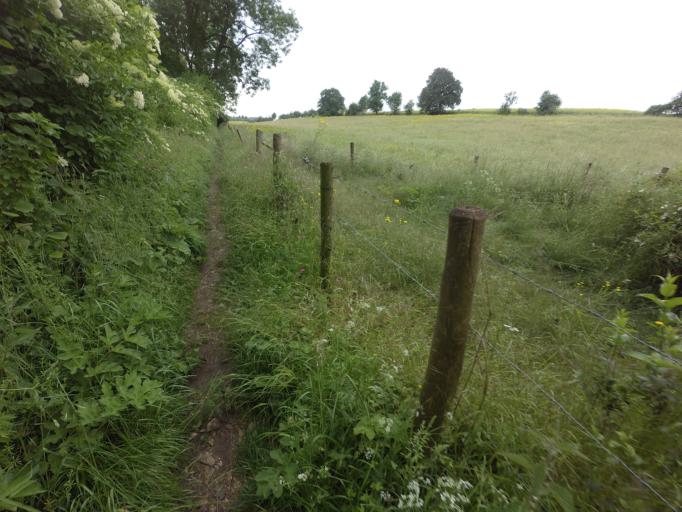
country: NL
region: Limburg
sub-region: Gemeente Voerendaal
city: Ubachsberg
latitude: 50.8538
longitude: 5.9670
